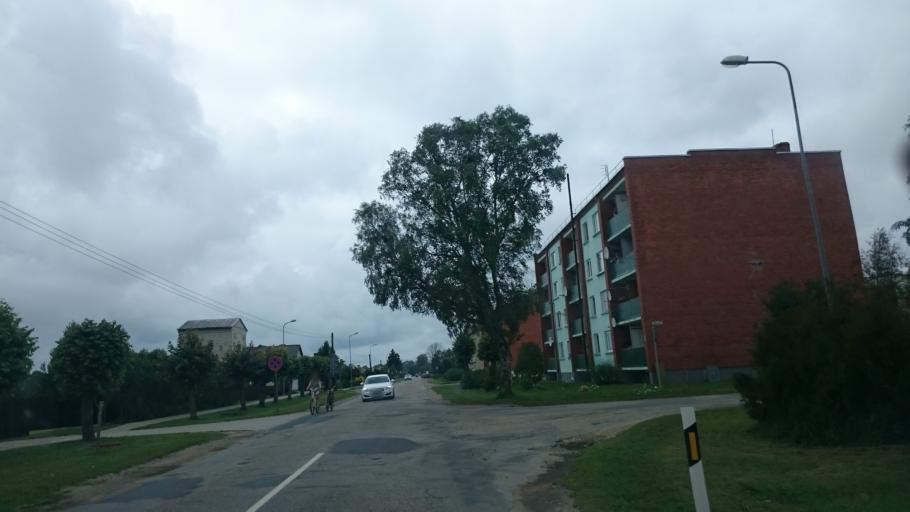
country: LV
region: Pavilostas
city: Pavilosta
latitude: 56.8834
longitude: 21.2027
